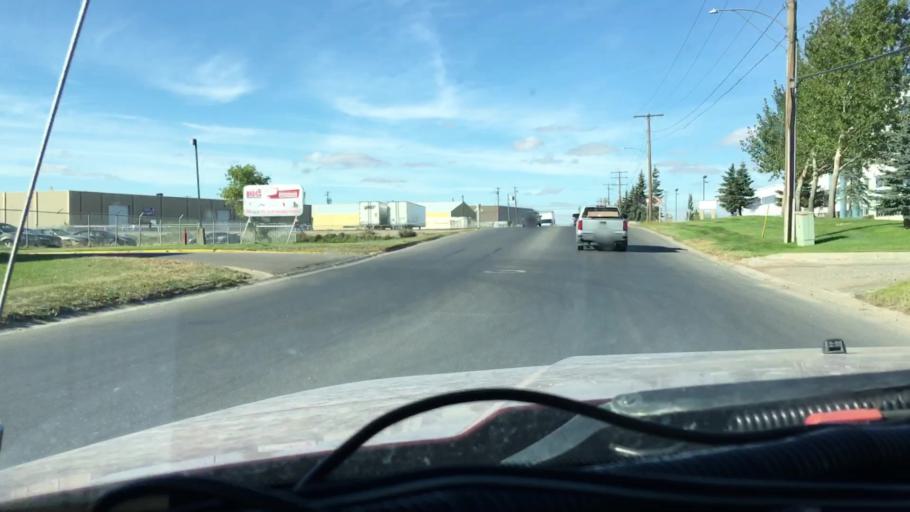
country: CA
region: Saskatchewan
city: Regina
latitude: 50.4730
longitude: -104.5615
